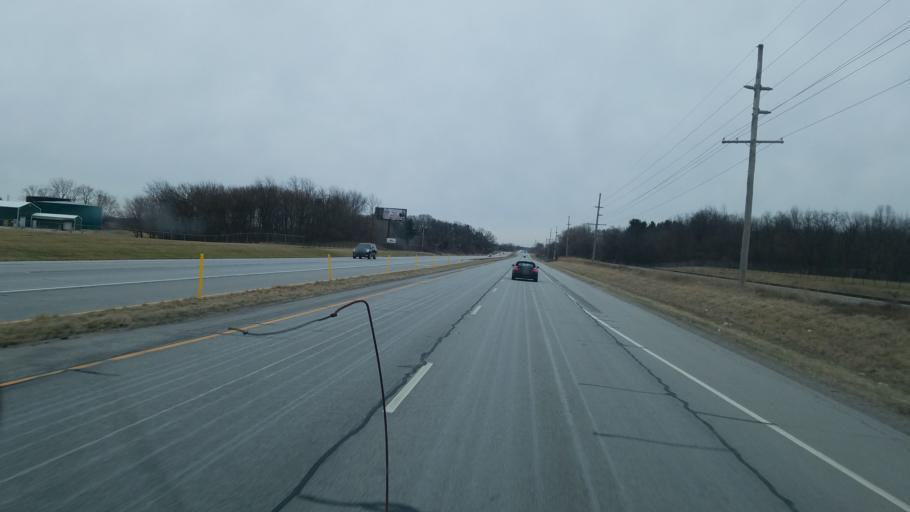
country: US
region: Indiana
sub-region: Porter County
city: Valparaiso
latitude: 41.4431
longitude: -86.9881
